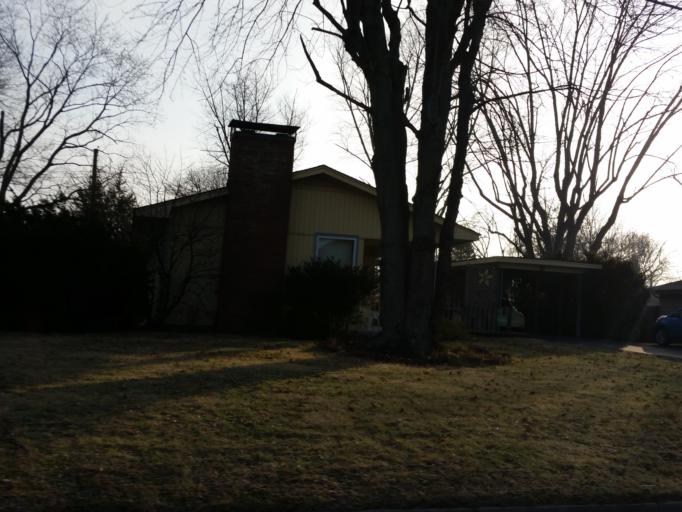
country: US
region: Indiana
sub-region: Bartholomew County
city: Columbus
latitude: 39.2255
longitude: -85.9085
